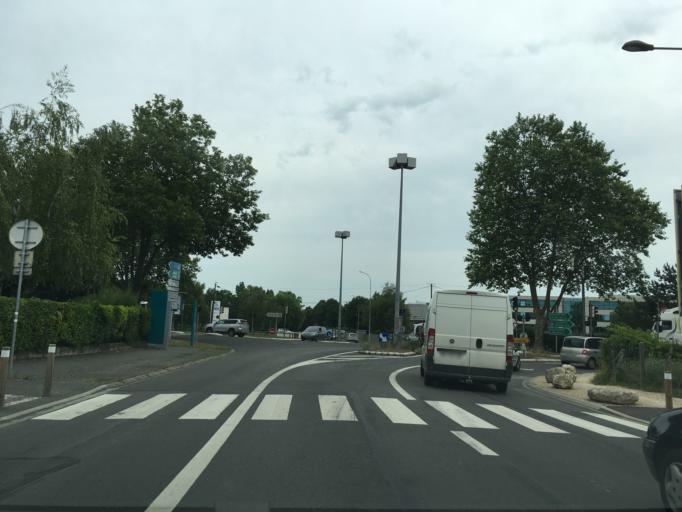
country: FR
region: Poitou-Charentes
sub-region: Departement des Deux-Sevres
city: Niort
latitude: 46.3099
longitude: -0.4827
